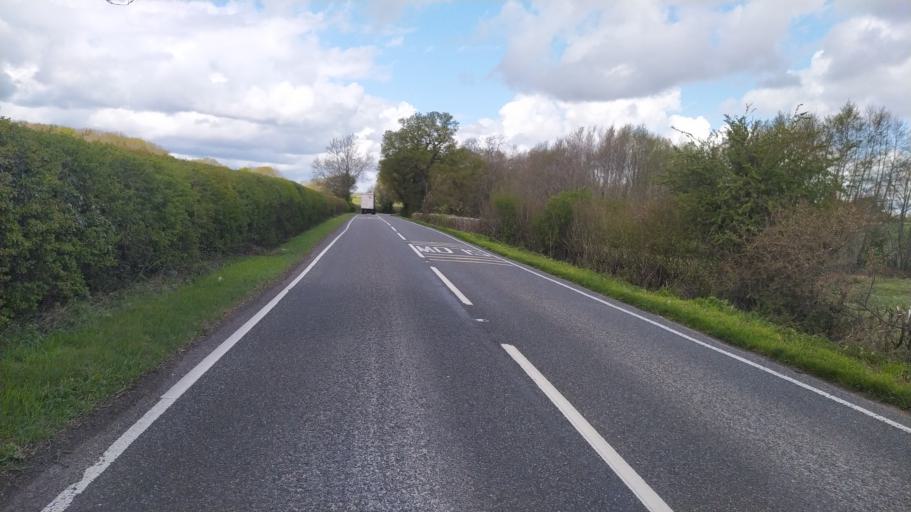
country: GB
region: England
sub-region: Somerset
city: Frome
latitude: 51.1790
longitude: -2.3095
